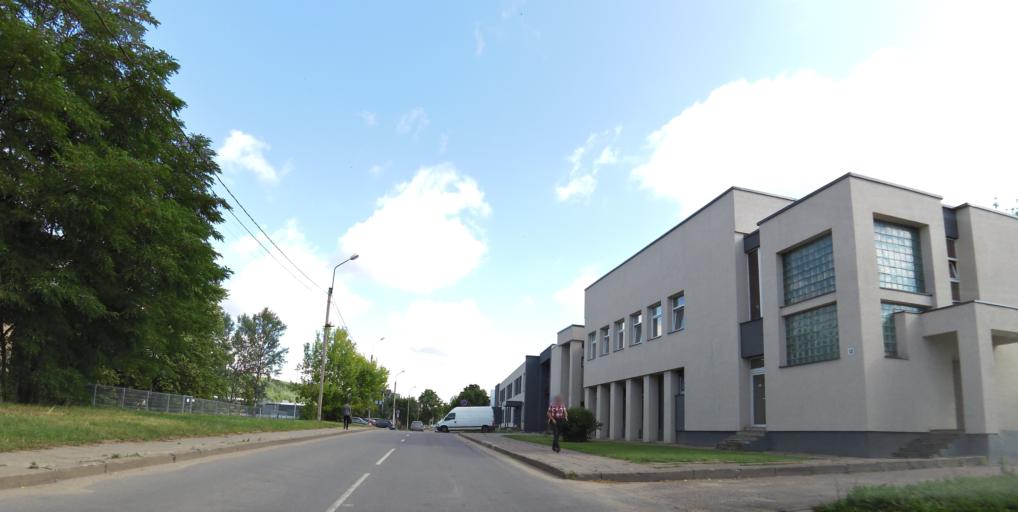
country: LT
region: Vilnius County
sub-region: Vilnius
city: Vilnius
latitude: 54.7013
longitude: 25.2700
